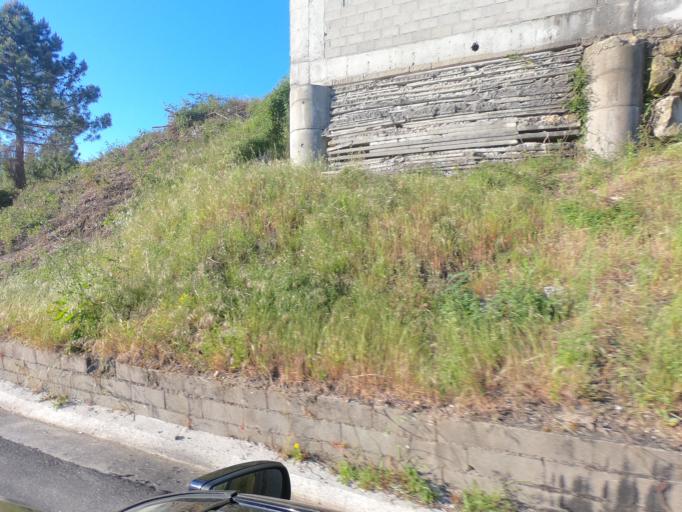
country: PT
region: Vila Real
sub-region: Vila Real
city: Vila Real
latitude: 41.3450
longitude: -7.7254
